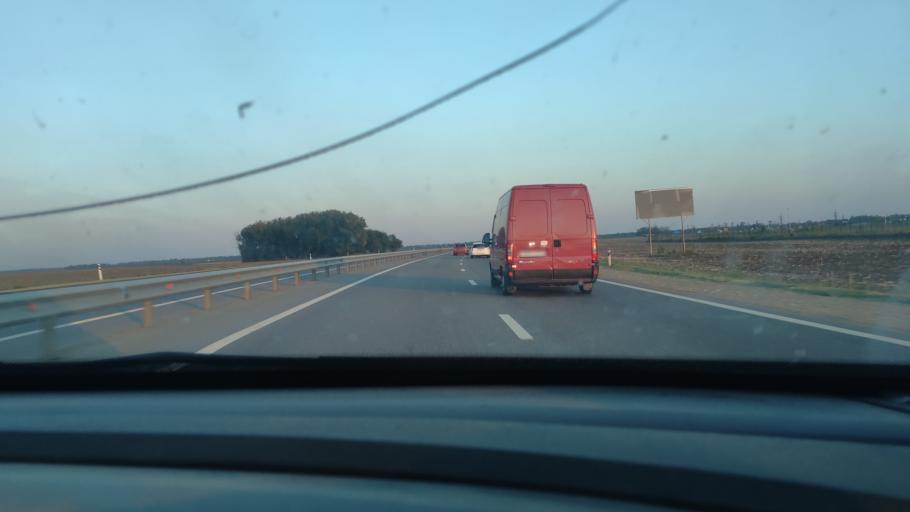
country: RU
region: Krasnodarskiy
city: Timashevsk
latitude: 45.6354
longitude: 38.9769
